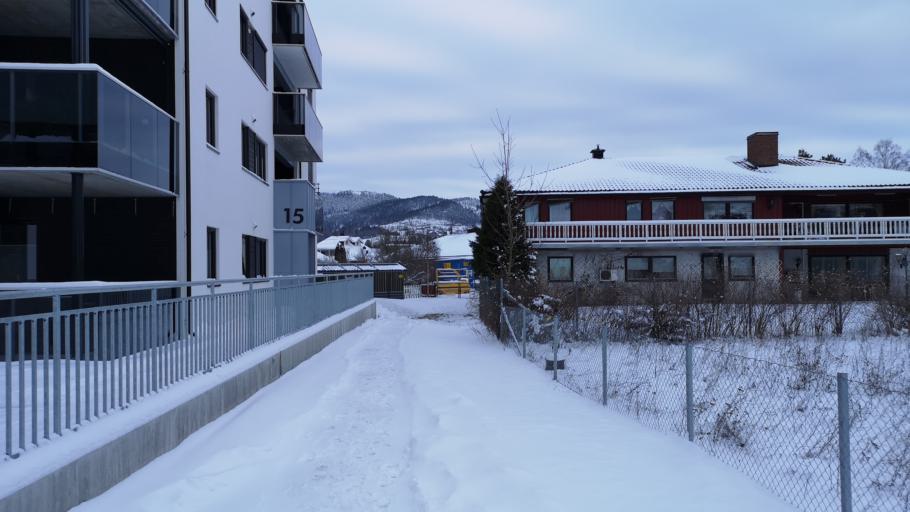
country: NO
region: Buskerud
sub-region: Ovre Eiker
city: Hokksund
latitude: 59.7690
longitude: 9.9121
